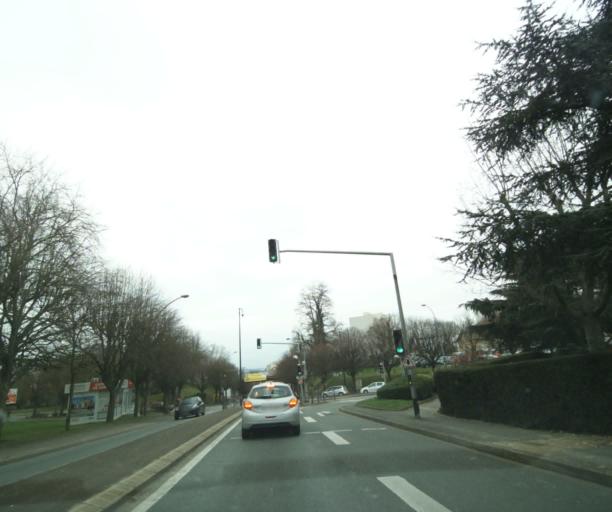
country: FR
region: Ile-de-France
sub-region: Departement des Yvelines
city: Poissy
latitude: 48.9260
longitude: 2.0517
